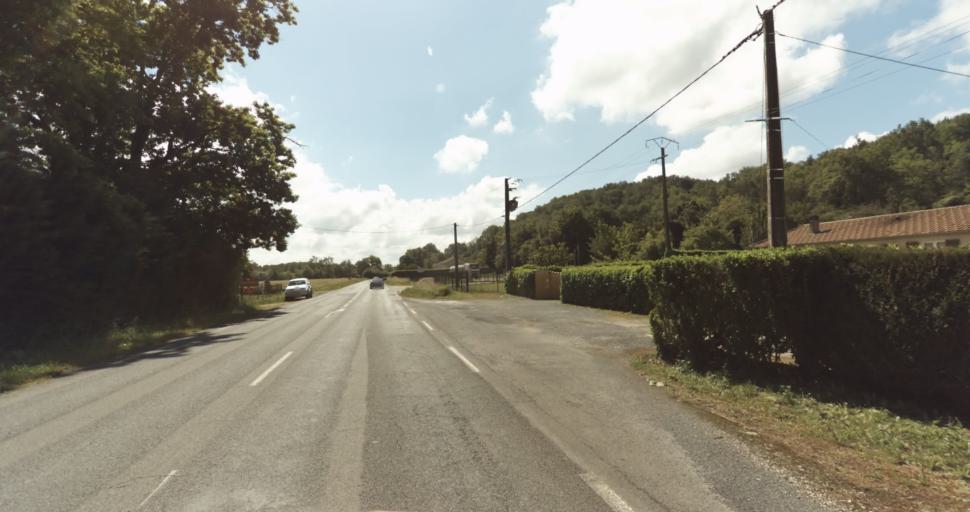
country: FR
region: Aquitaine
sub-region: Departement de la Dordogne
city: Le Bugue
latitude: 44.8431
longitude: 0.9260
